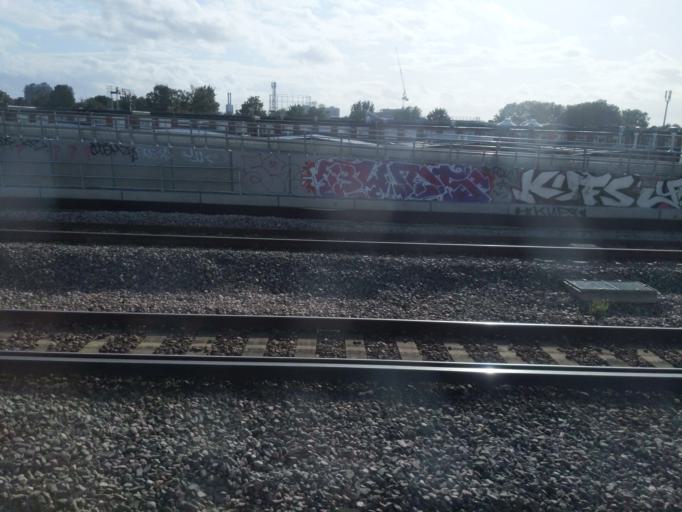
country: GB
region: England
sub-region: Greater London
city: Bethnal Green
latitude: 51.4894
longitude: -0.0530
